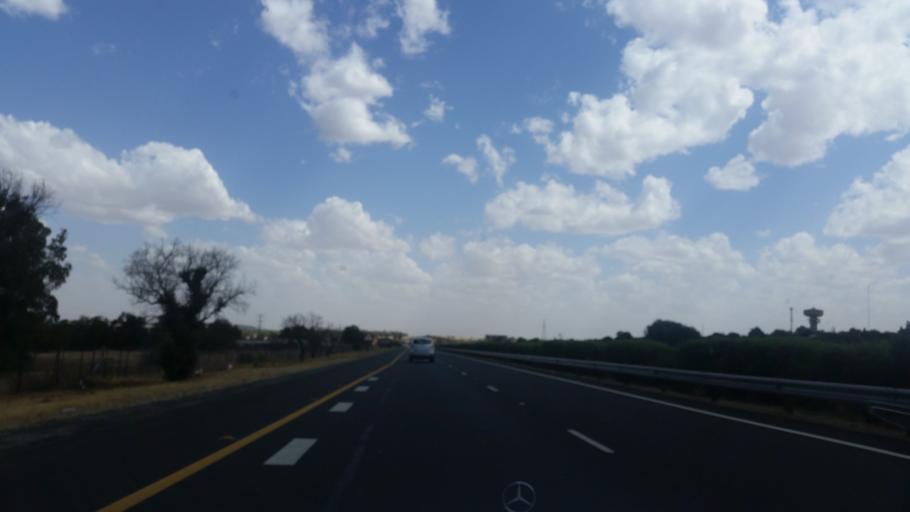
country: ZA
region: Orange Free State
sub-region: Mangaung Metropolitan Municipality
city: Bloemfontein
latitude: -29.0792
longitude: 26.1791
